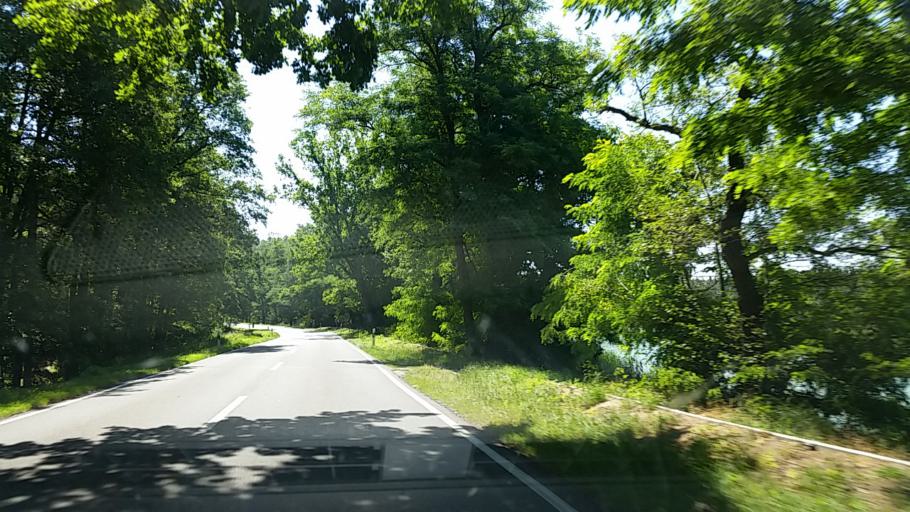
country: DE
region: Saxony-Anhalt
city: Pretzsch
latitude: 51.6816
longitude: 12.8036
